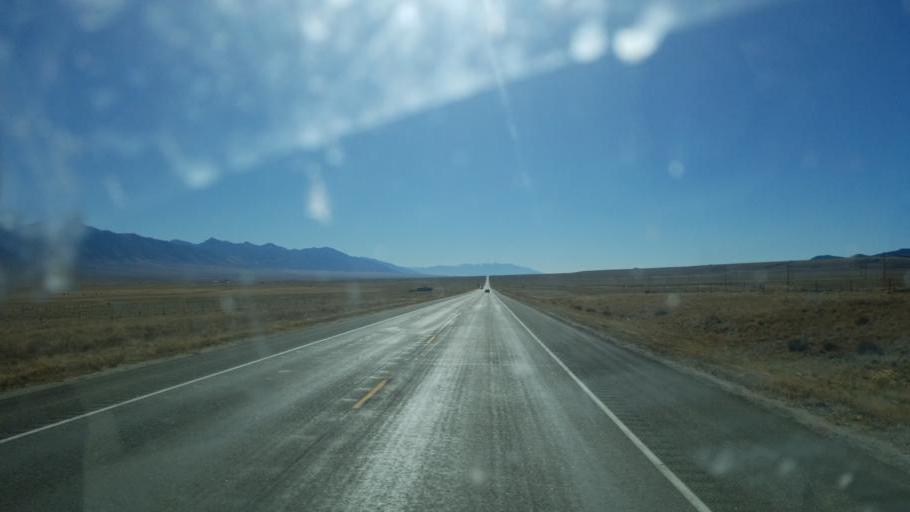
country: US
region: Colorado
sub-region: Chaffee County
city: Salida
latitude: 38.3296
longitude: -106.0100
